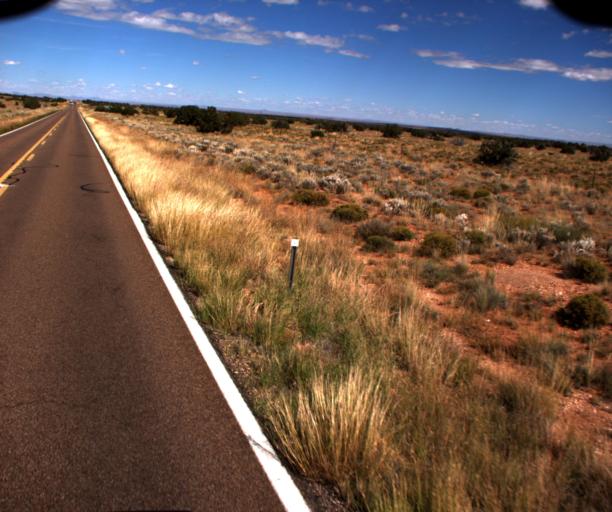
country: US
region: Arizona
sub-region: Navajo County
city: Holbrook
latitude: 34.6943
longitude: -110.3064
